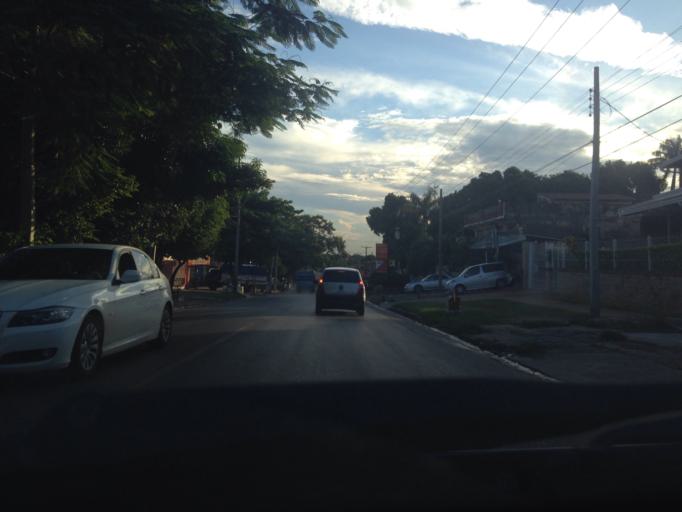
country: PY
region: Central
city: Lambare
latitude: -25.3293
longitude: -57.5855
